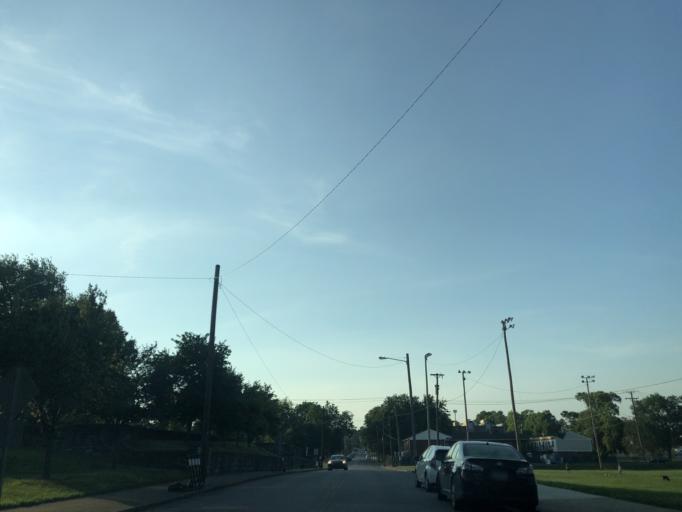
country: US
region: Tennessee
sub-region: Davidson County
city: Nashville
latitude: 36.1802
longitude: -86.7897
